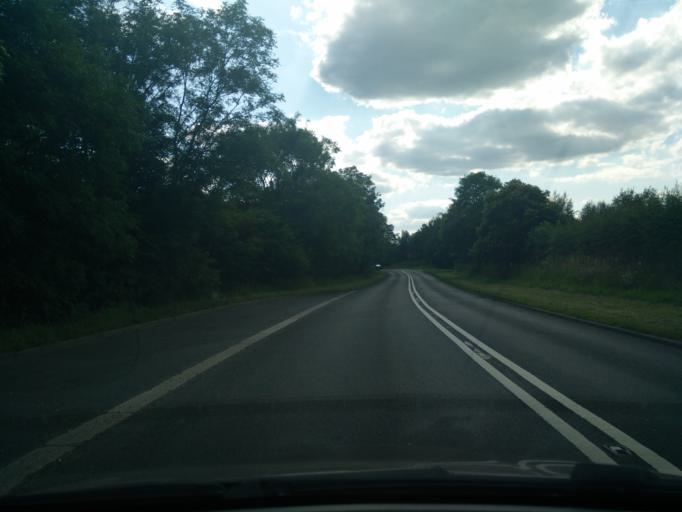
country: GB
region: England
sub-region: Derbyshire
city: West Hallam
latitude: 52.9561
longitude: -1.3390
